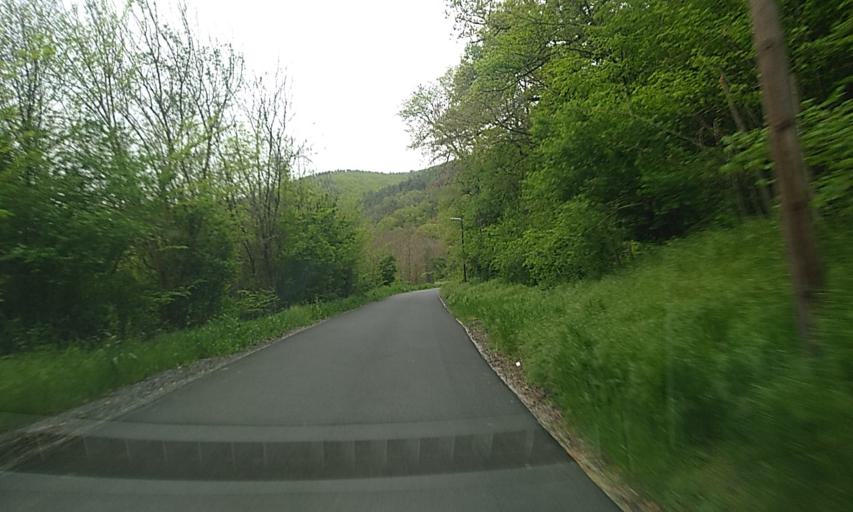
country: RS
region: Central Serbia
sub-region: Nisavski Okrug
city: Razanj
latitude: 43.6192
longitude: 21.5299
